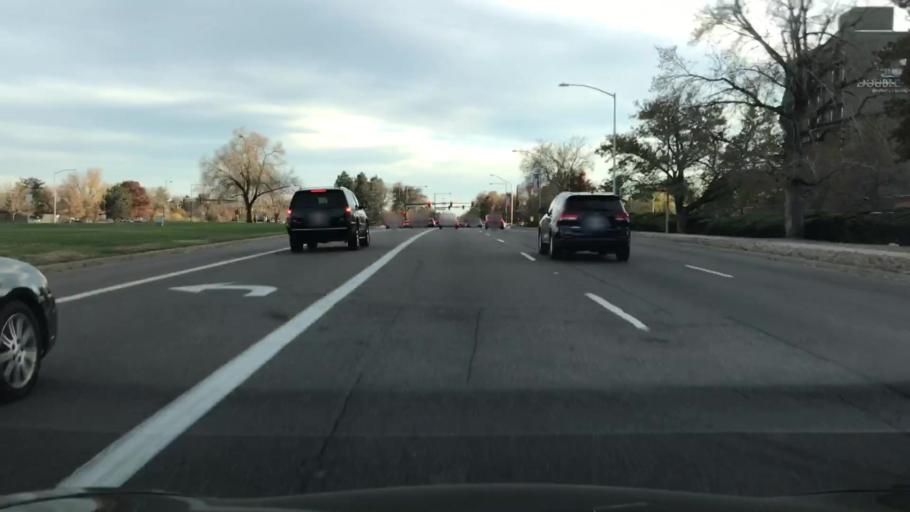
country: US
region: Colorado
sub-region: Adams County
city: Commerce City
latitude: 39.7638
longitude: -104.9034
